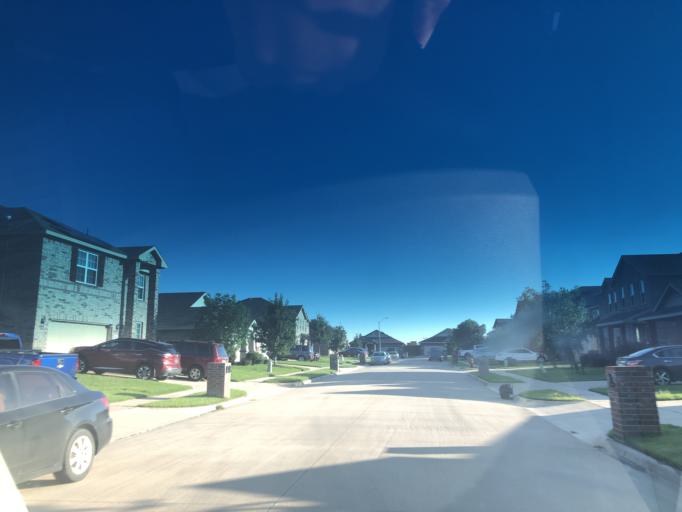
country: US
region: Texas
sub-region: Dallas County
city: Grand Prairie
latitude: 32.7061
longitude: -97.0169
